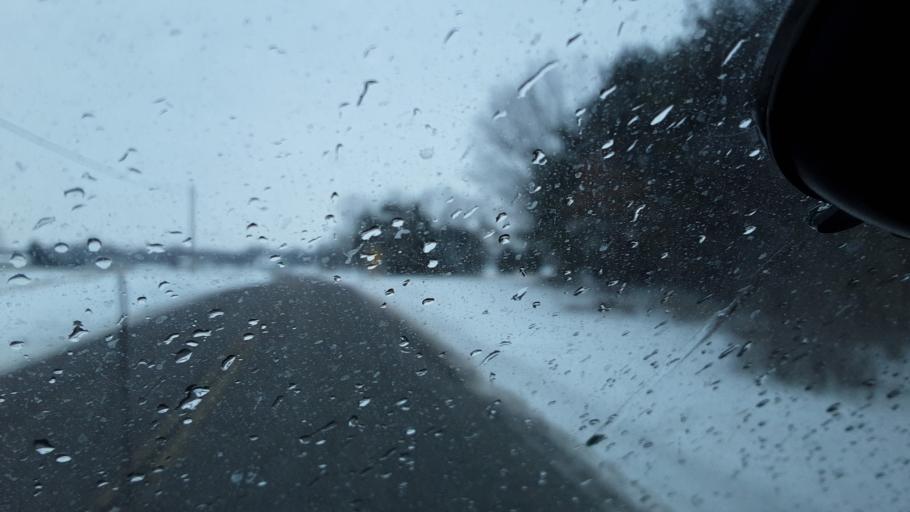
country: US
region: Ohio
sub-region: Licking County
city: Hebron
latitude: 39.9681
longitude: -82.4589
